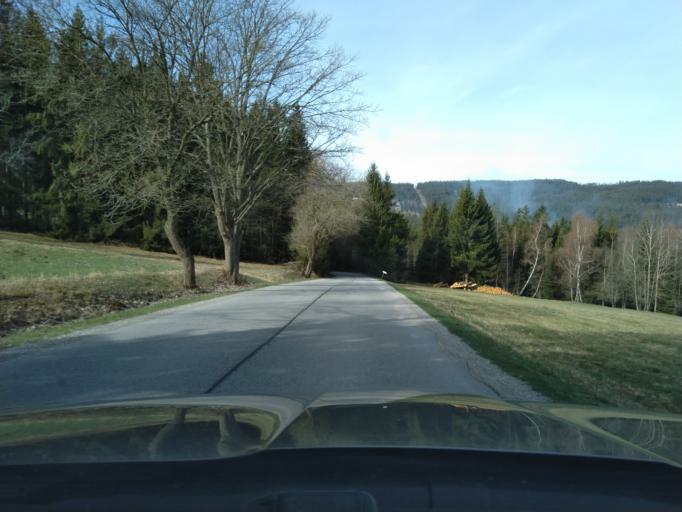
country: CZ
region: Jihocesky
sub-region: Okres Prachatice
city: Stachy
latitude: 49.0751
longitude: 13.6486
